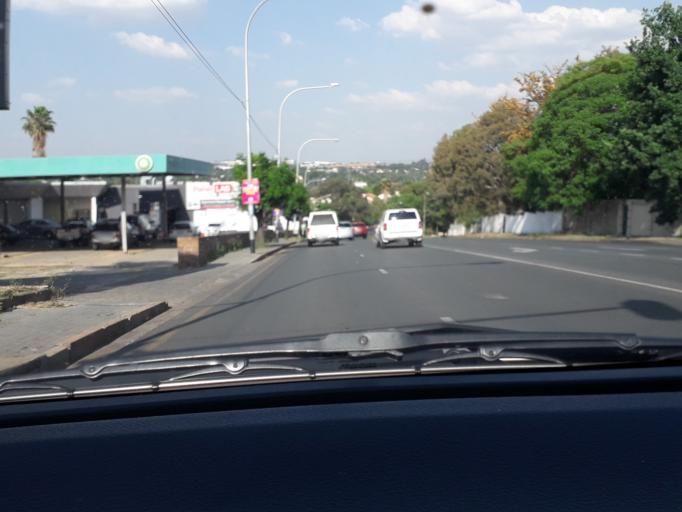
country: ZA
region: Gauteng
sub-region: City of Johannesburg Metropolitan Municipality
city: Modderfontein
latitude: -26.1262
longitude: 28.1084
